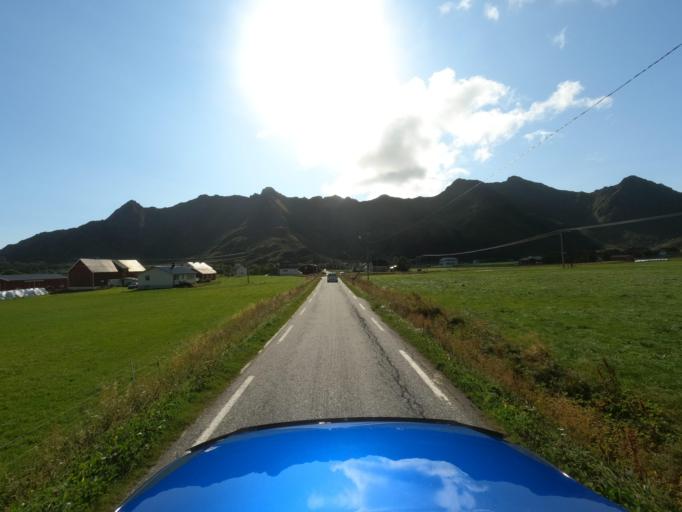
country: NO
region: Nordland
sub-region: Vestvagoy
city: Leknes
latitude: 68.1138
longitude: 13.7085
